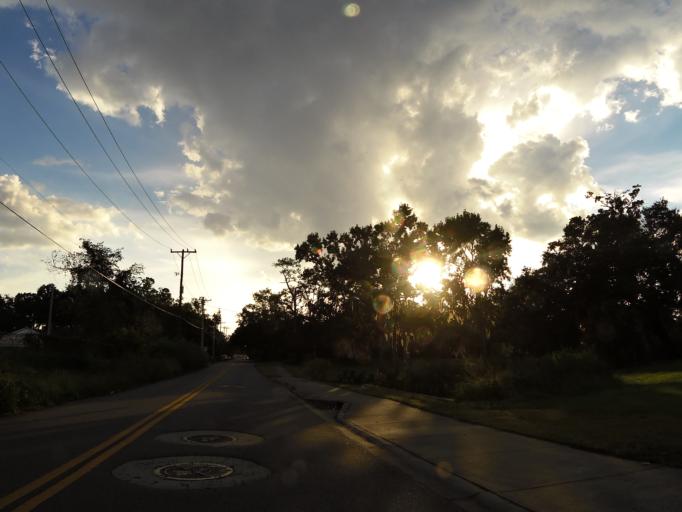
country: US
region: Florida
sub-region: Duval County
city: Jacksonville
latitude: 30.3333
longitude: -81.7006
